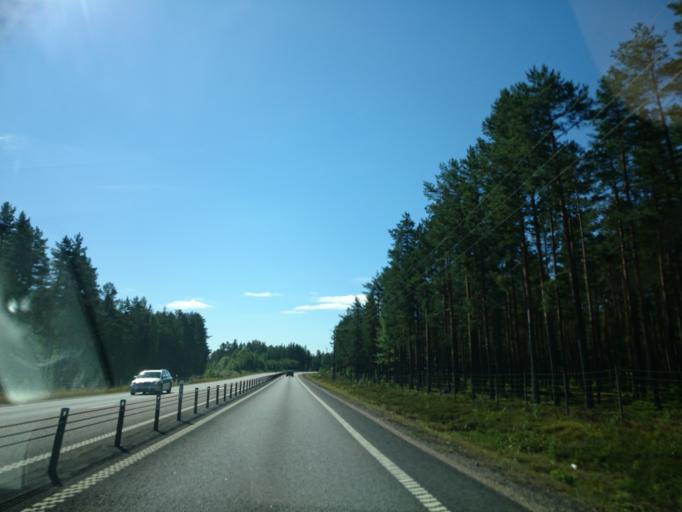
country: SE
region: Gaevleborg
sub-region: Gavle Kommun
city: Norrsundet
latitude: 61.0331
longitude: 16.9719
